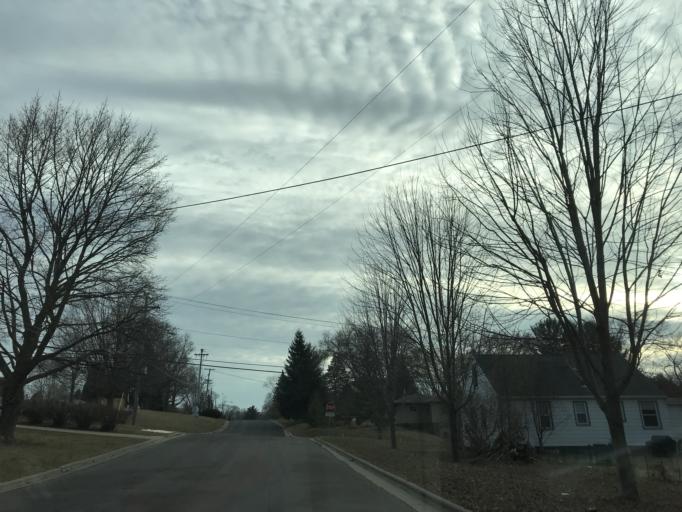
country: US
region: Wisconsin
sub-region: Dane County
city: Monona
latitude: 43.0629
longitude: -89.3360
